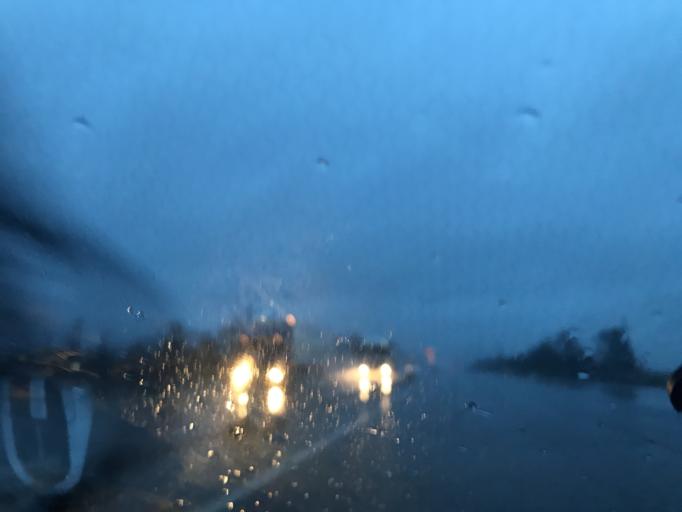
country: RU
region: Rostov
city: Samarskoye
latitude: 47.0158
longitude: 39.7349
